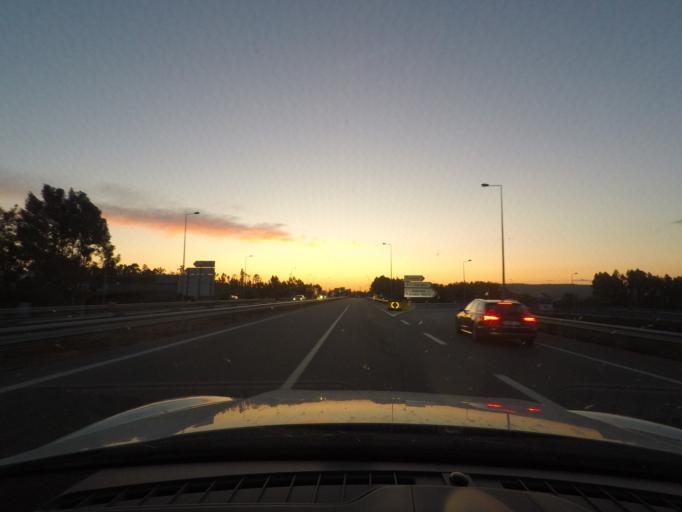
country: PT
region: Porto
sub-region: Pacos de Ferreira
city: Ferreira
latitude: 41.2586
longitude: -8.3629
